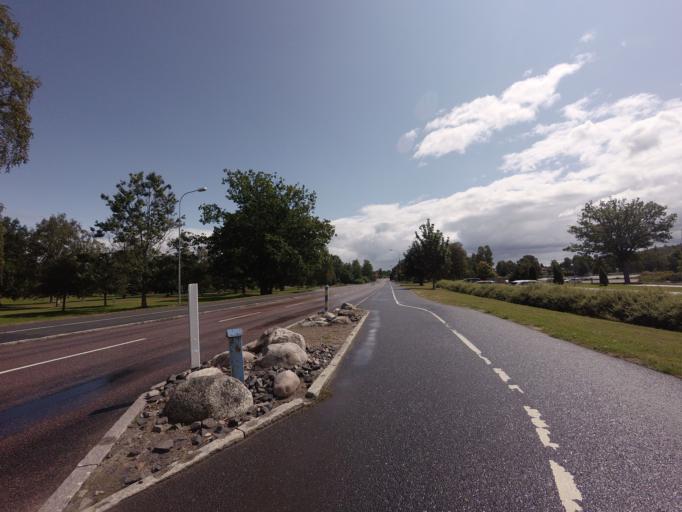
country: SE
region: Skane
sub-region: Osby Kommun
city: Osby
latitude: 56.3791
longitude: 13.9993
